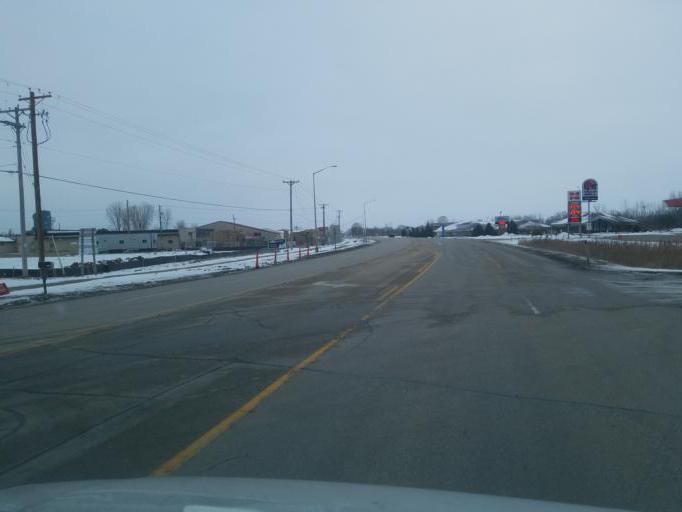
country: US
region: Wisconsin
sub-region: Waupaca County
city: New London
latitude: 44.4055
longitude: -88.7420
